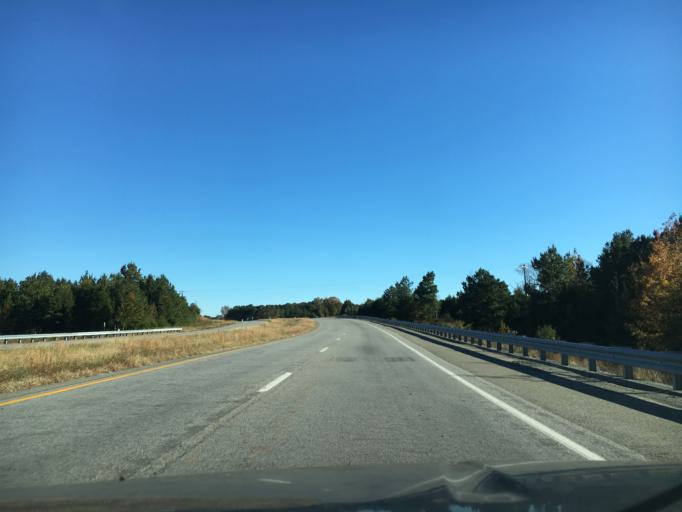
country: US
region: Virginia
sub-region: Mecklenburg County
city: Clarksville
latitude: 36.6087
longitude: -78.5771
